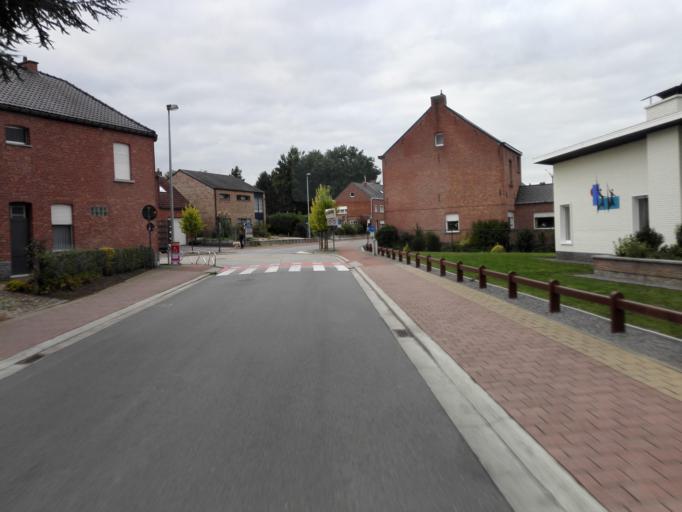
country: BE
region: Flanders
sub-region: Provincie Vlaams-Brabant
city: Boortmeerbeek
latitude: 50.9896
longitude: 4.5578
